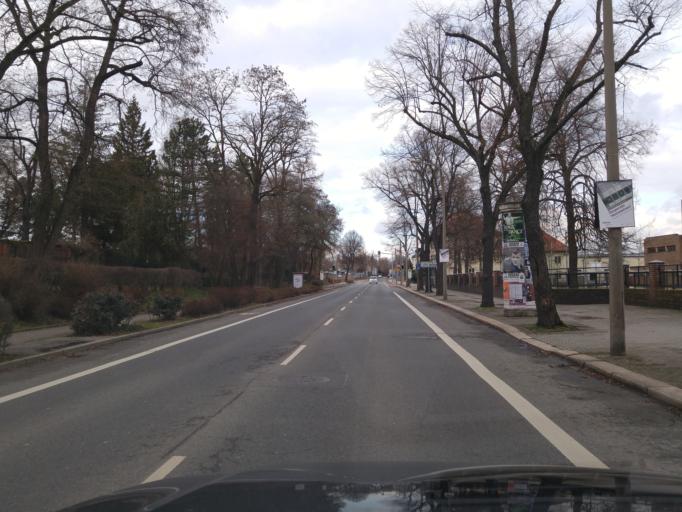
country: DE
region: Saxony
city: Zwickau
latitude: 50.7296
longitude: 12.4835
